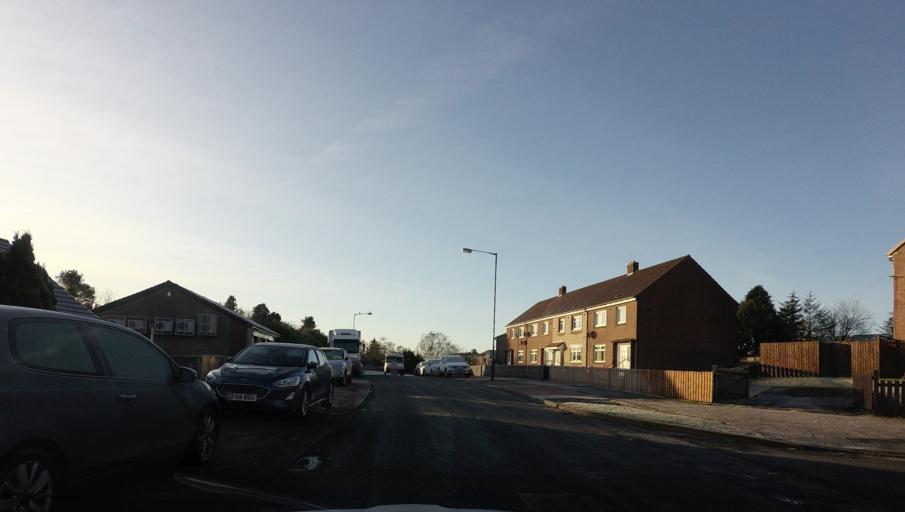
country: GB
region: Scotland
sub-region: North Lanarkshire
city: Shotts
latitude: 55.8249
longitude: -3.8011
